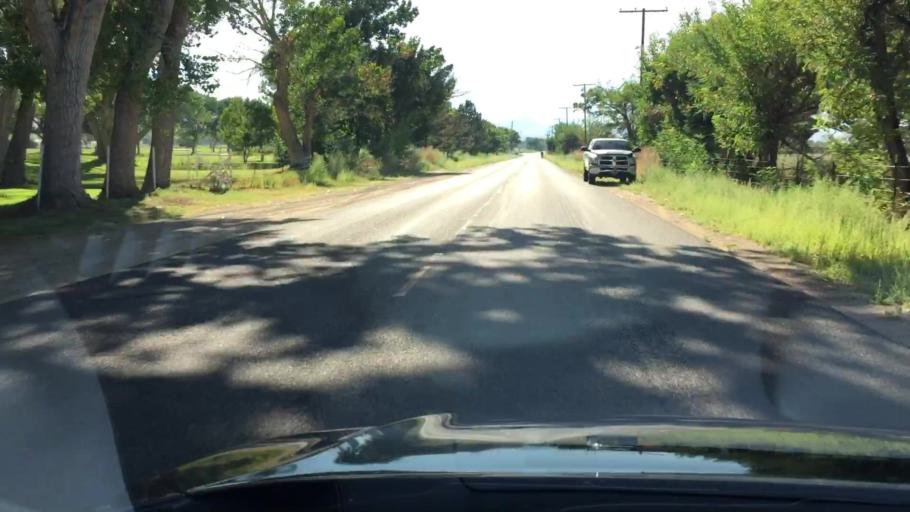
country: US
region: California
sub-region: Inyo County
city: Bishop
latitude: 37.3468
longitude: -118.3996
